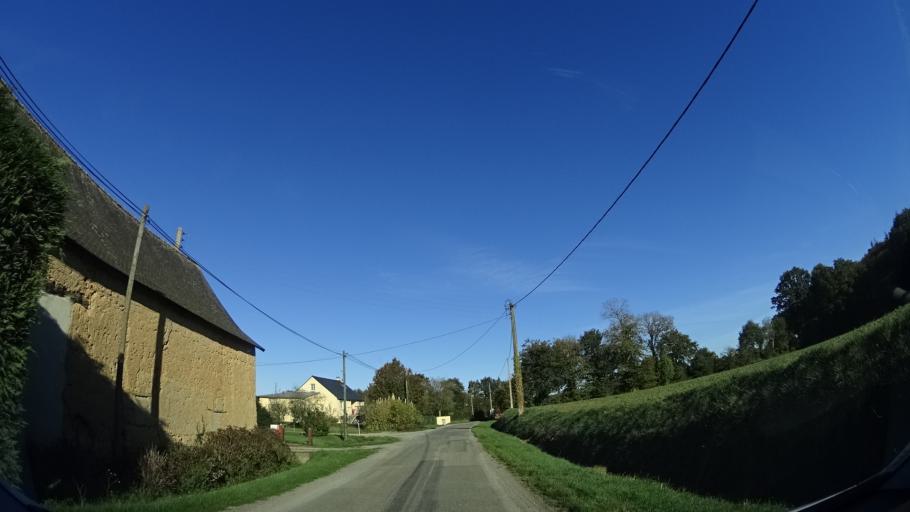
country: FR
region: Brittany
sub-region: Departement d'Ille-et-Vilaine
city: Geveze
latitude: 48.2076
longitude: -1.7744
